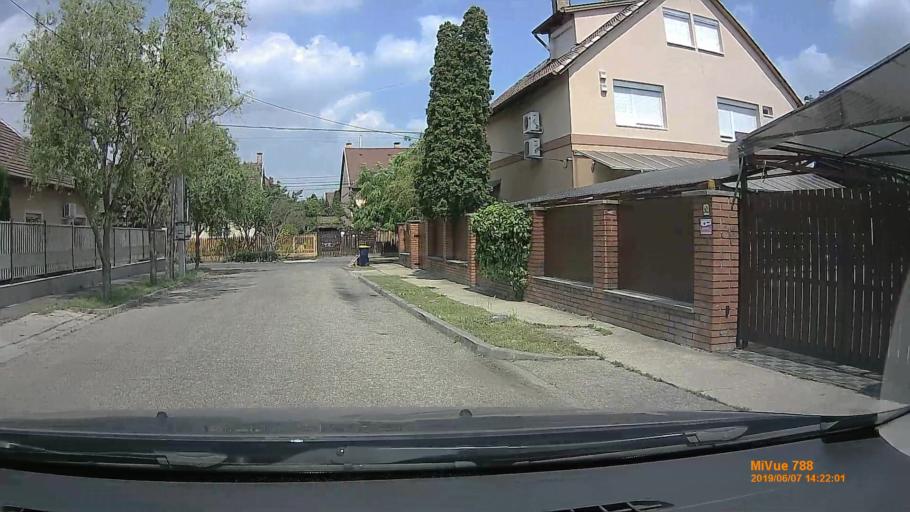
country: HU
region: Budapest
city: Budapest XIX. keruelet
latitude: 47.4344
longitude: 19.1380
